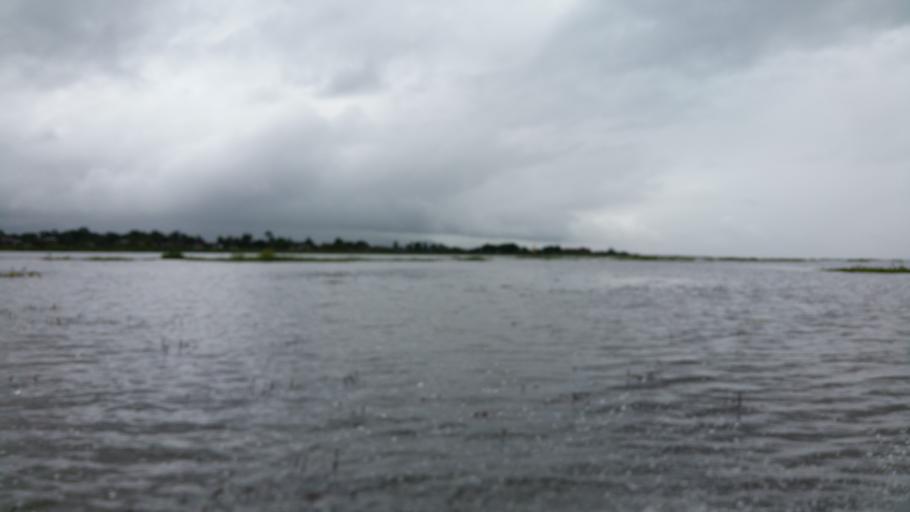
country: MM
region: Shan
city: Taunggyi
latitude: 20.5283
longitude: 96.8987
